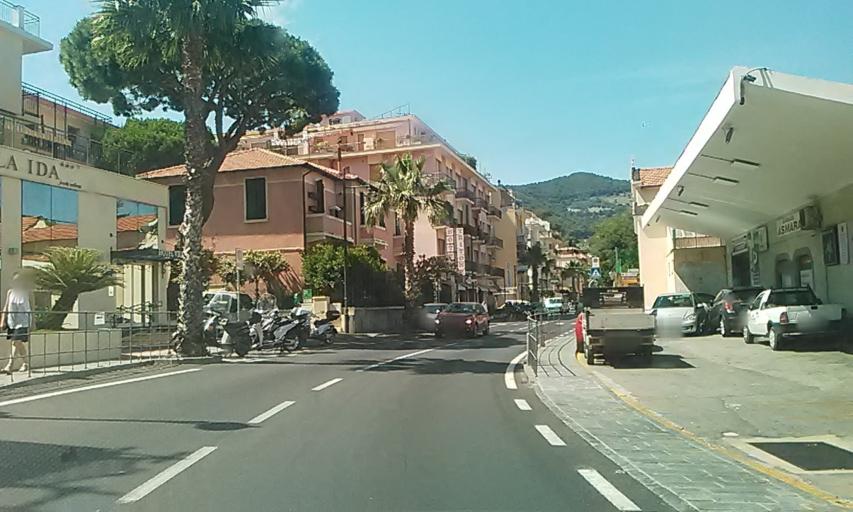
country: IT
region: Liguria
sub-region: Provincia di Savona
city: Laigueglia
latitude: 43.9752
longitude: 8.1583
